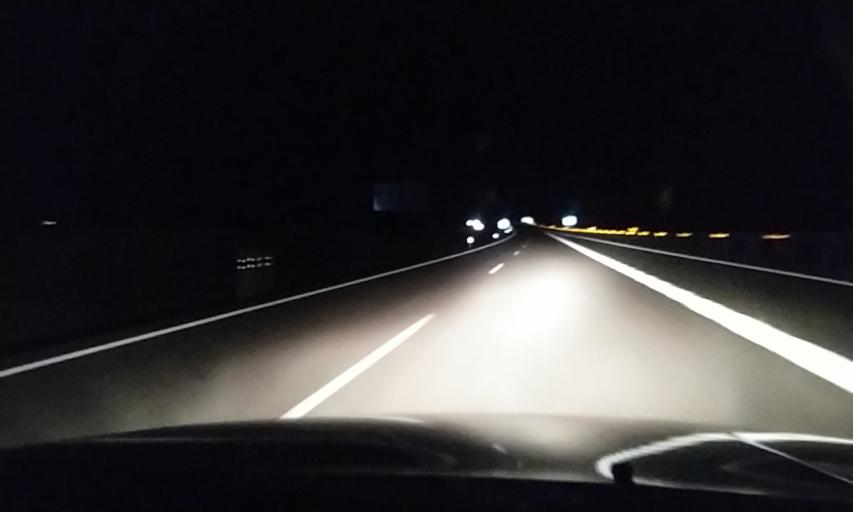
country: ES
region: Castille and Leon
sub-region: Provincia de Leon
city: La Baneza
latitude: 42.2853
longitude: -5.9122
